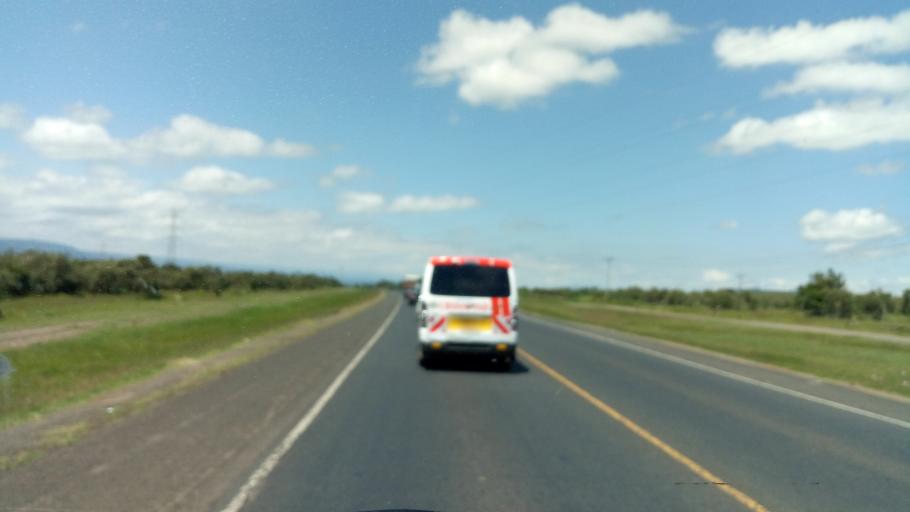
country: KE
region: Nakuru
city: Naivasha
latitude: -0.5370
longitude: 36.3350
